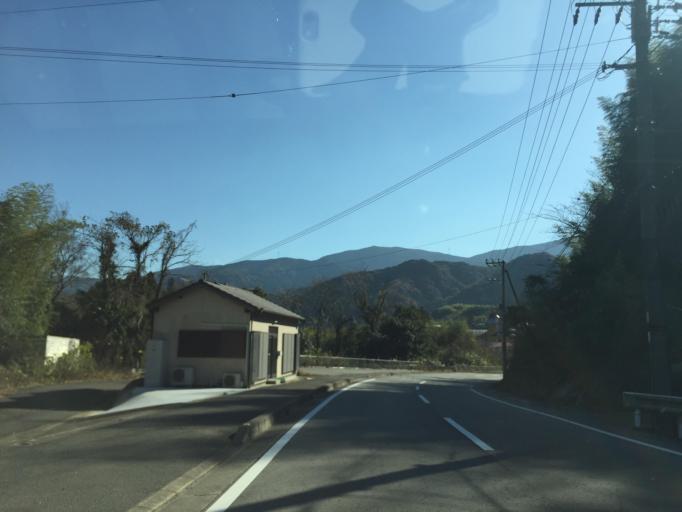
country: JP
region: Wakayama
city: Iwade
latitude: 34.1506
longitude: 135.3457
